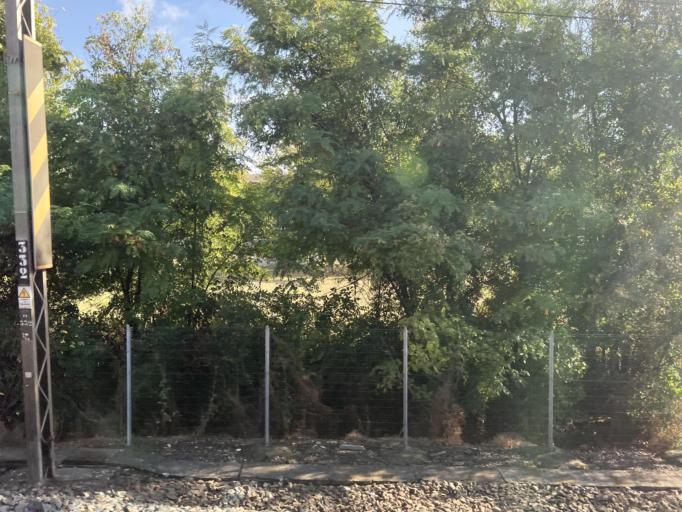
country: IT
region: Emilia-Romagna
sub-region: Provincia di Parma
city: Parma
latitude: 44.8143
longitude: 10.3000
